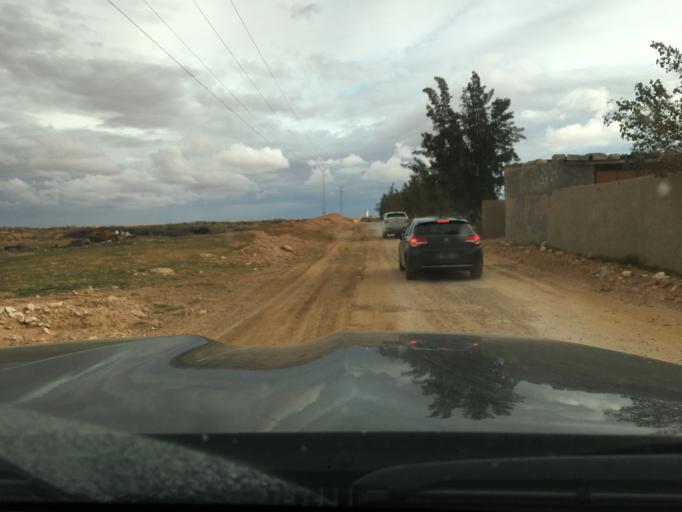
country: TN
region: Madanin
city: Medenine
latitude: 33.2743
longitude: 10.5634
